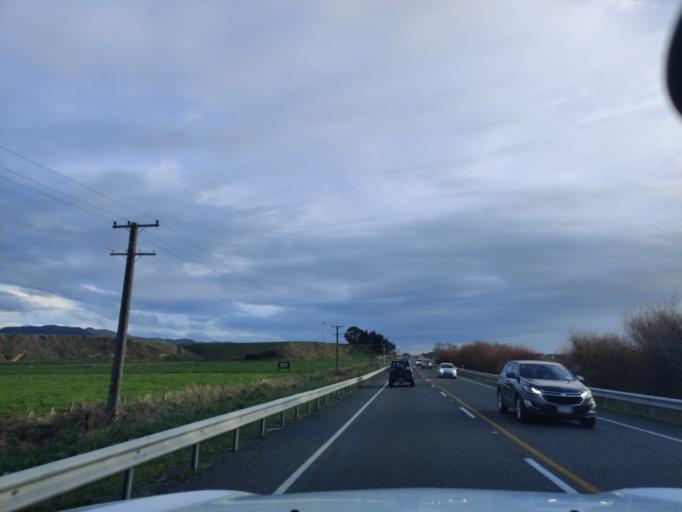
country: NZ
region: Manawatu-Wanganui
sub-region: Horowhenua District
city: Foxton
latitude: -40.5333
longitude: 175.4307
